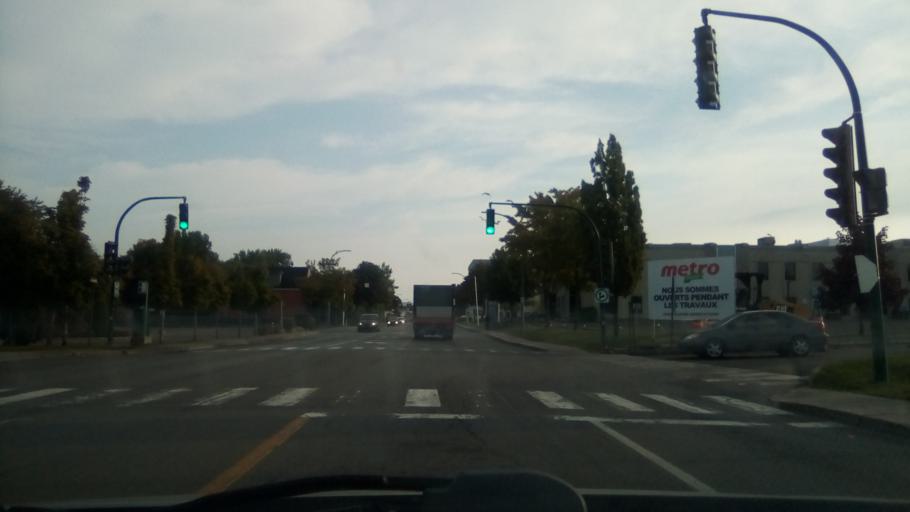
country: CA
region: Quebec
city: Mont-Royal
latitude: 45.5212
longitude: -73.6253
